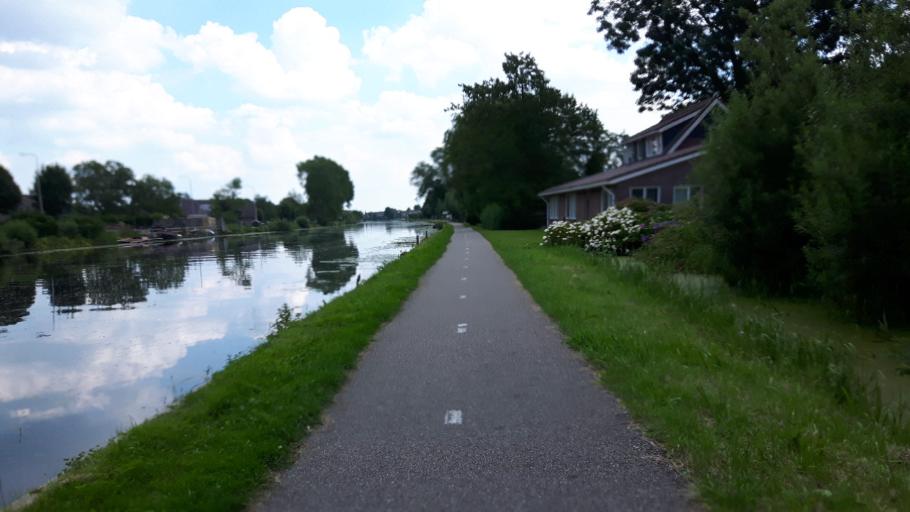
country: NL
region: South Holland
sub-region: Bodegraven-Reeuwijk
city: Bodegraven
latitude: 52.0834
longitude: 4.7999
